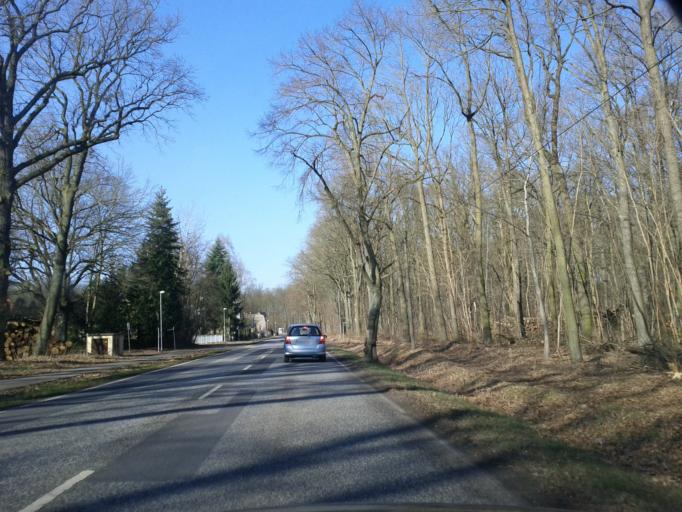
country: DE
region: Brandenburg
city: Spreenhagen
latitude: 52.3952
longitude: 13.9322
